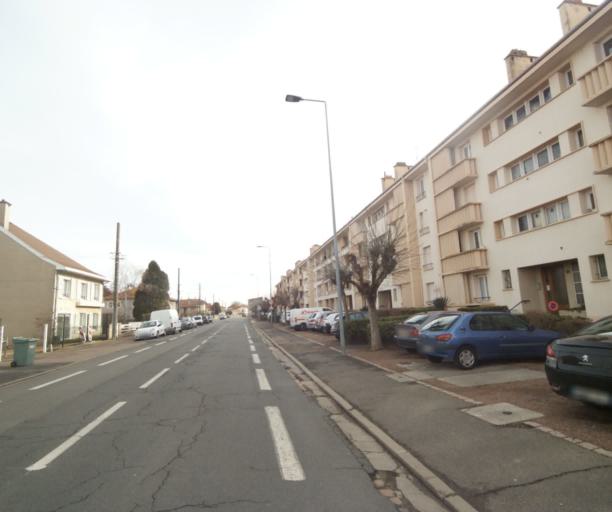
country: FR
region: Rhone-Alpes
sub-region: Departement de la Loire
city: Riorges
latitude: 46.0238
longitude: 4.0509
